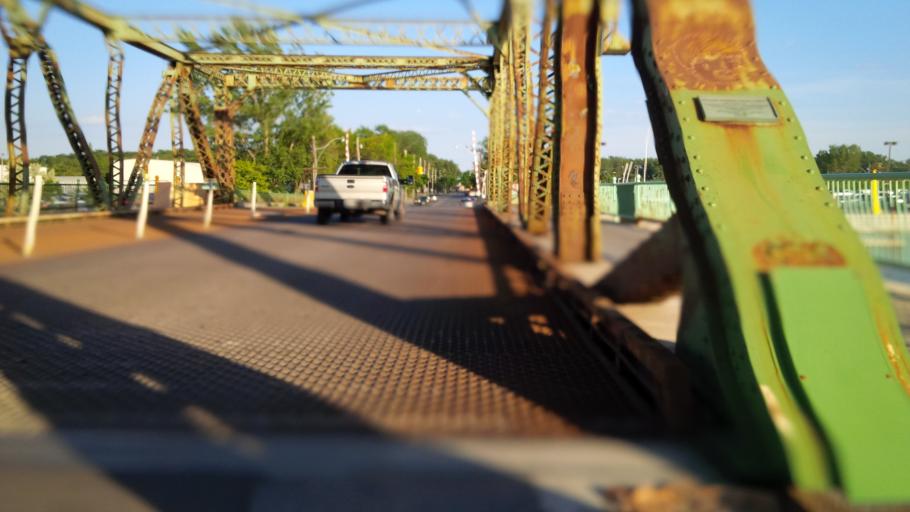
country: CA
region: Ontario
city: Toronto
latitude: 43.6414
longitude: -79.3493
